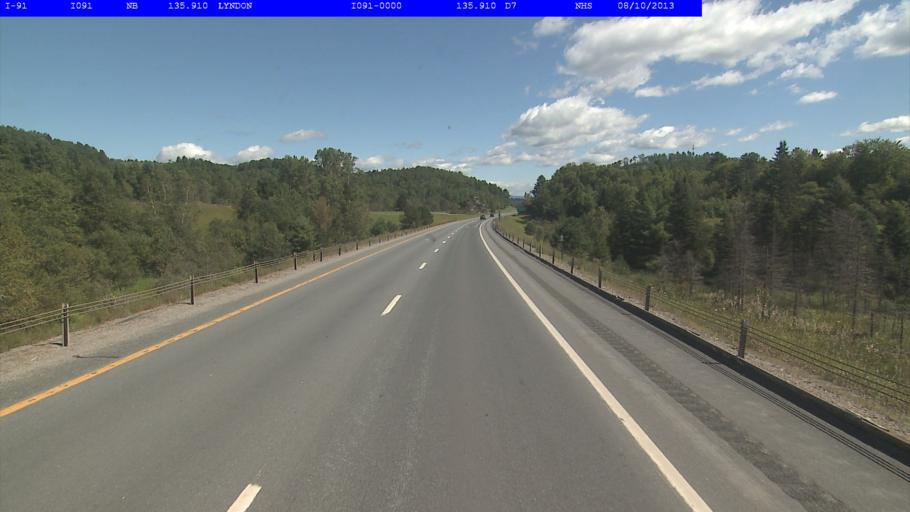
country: US
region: Vermont
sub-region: Caledonia County
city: Lyndon
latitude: 44.5015
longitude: -72.0187
